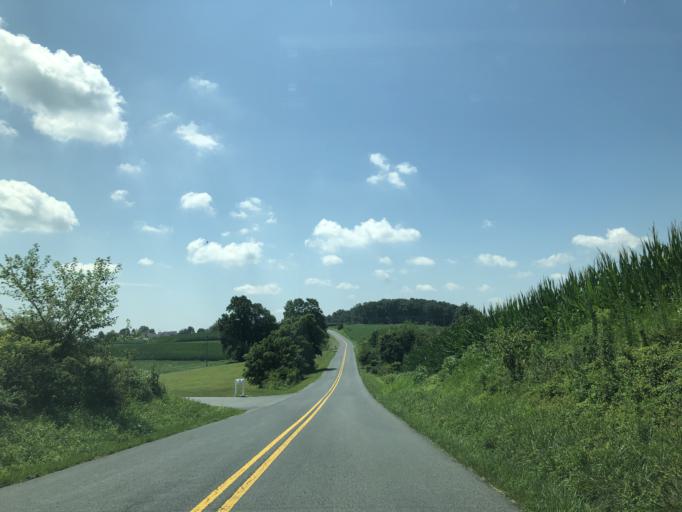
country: US
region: Maryland
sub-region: Carroll County
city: Westminster
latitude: 39.5266
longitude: -76.9876
